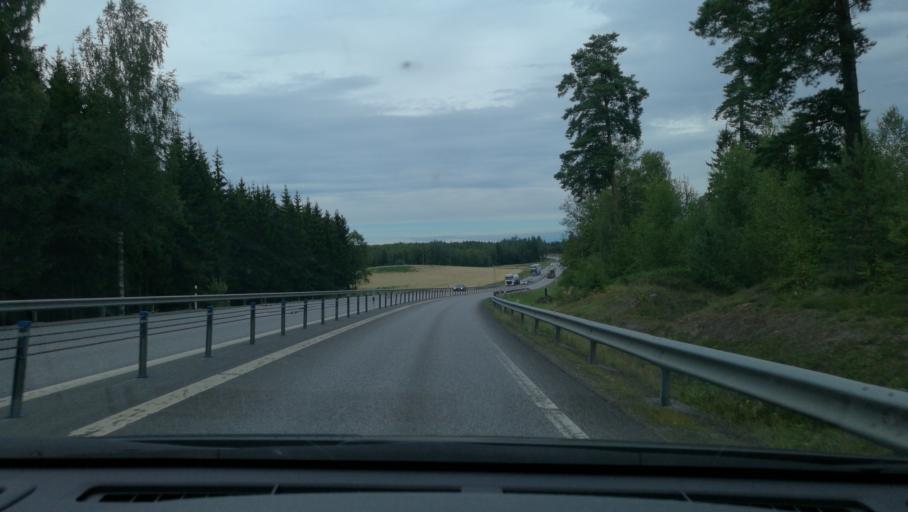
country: SE
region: Soedermanland
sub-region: Katrineholms Kommun
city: Katrineholm
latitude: 58.8409
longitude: 16.1963
